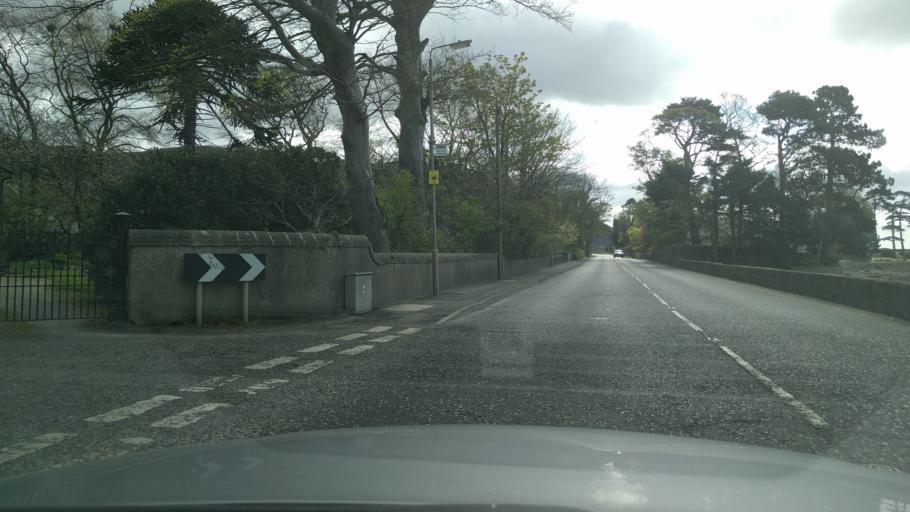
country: GB
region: Northern Ireland
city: Rostrevor
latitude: 54.1004
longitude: -6.2142
